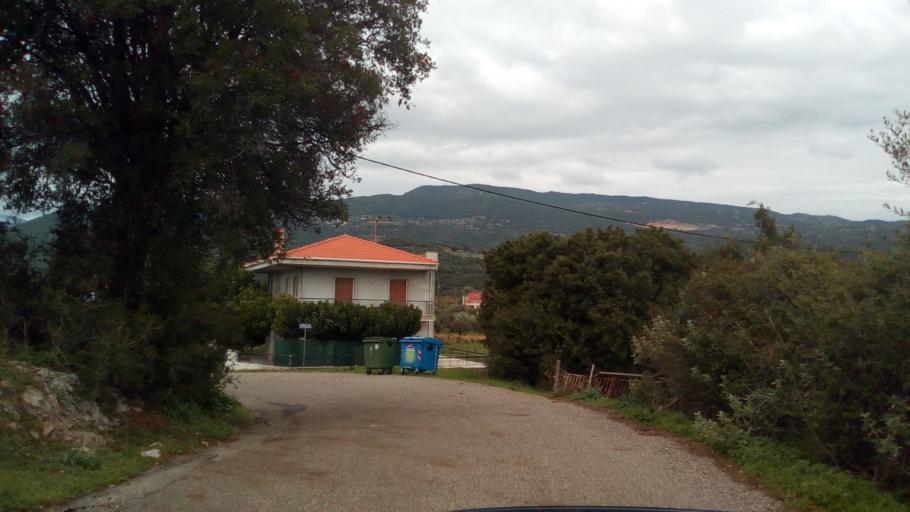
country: GR
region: West Greece
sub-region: Nomos Achaias
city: Kamarai
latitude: 38.4144
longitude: 21.9531
